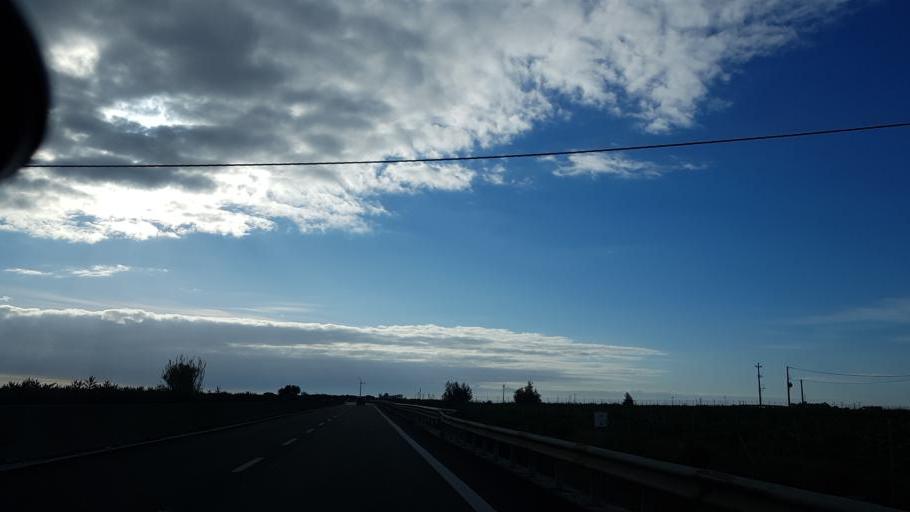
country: IT
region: Apulia
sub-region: Provincia di Brindisi
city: La Rosa
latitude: 40.5875
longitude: 17.9741
